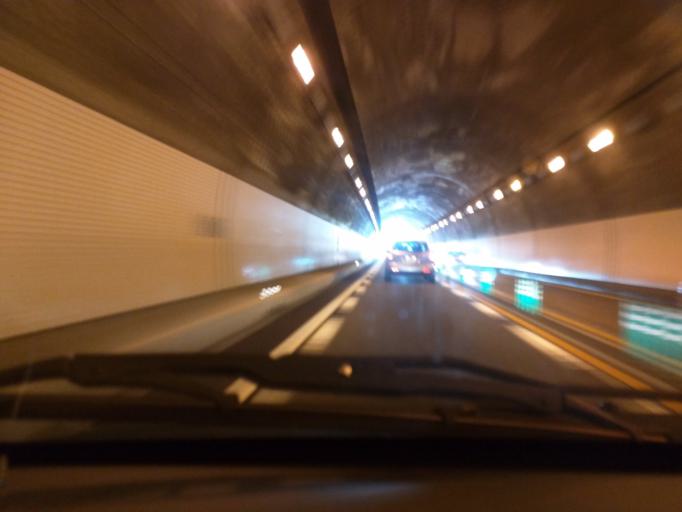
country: JP
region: Niigata
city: Arai
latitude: 37.0477
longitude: 138.2326
